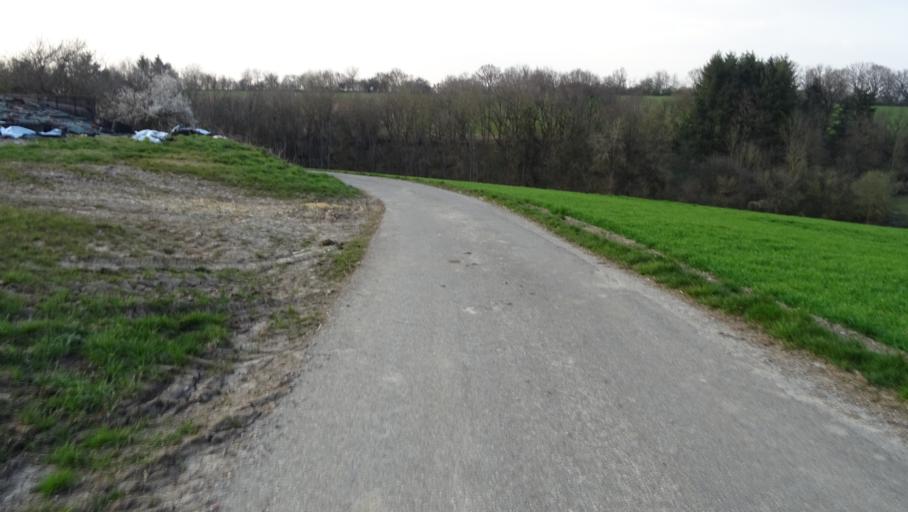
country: DE
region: Baden-Wuerttemberg
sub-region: Karlsruhe Region
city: Seckach
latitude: 49.4015
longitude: 9.2899
